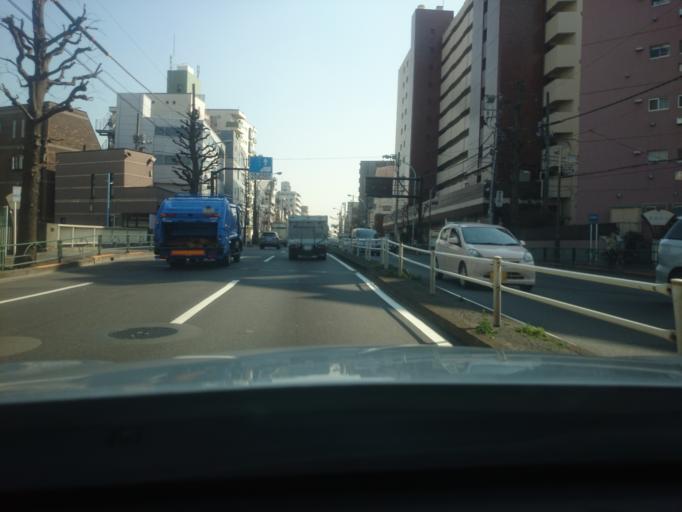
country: JP
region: Tokyo
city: Musashino
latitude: 35.7015
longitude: 139.6168
